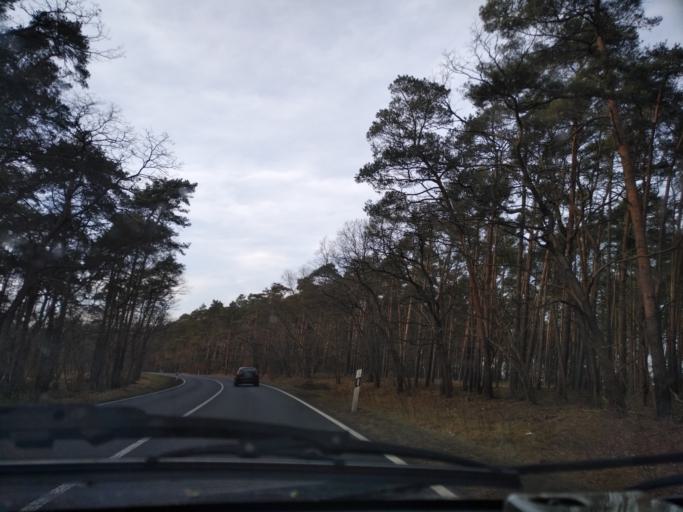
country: DE
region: Brandenburg
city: Herzberg
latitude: 51.7305
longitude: 13.2197
